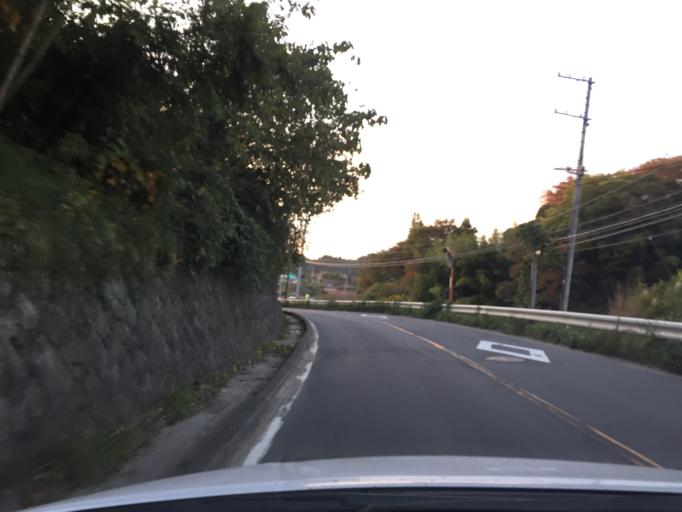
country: JP
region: Fukushima
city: Koriyama
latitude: 37.3687
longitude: 140.4468
